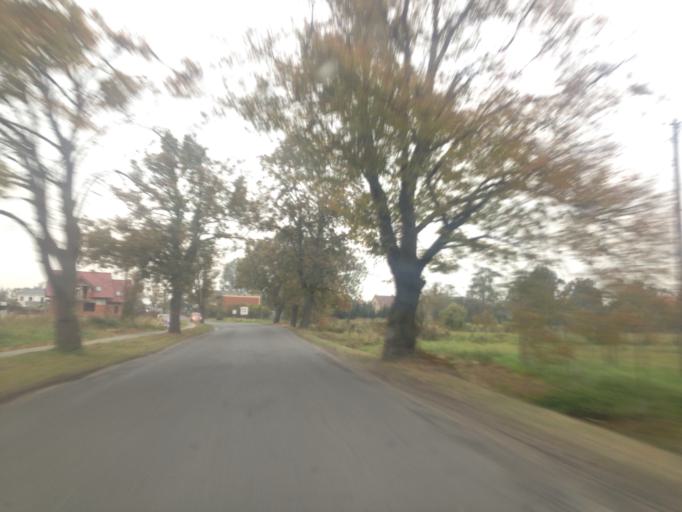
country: PL
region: Greater Poland Voivodeship
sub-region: Powiat poznanski
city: Kleszczewo
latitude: 52.3628
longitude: 17.1294
